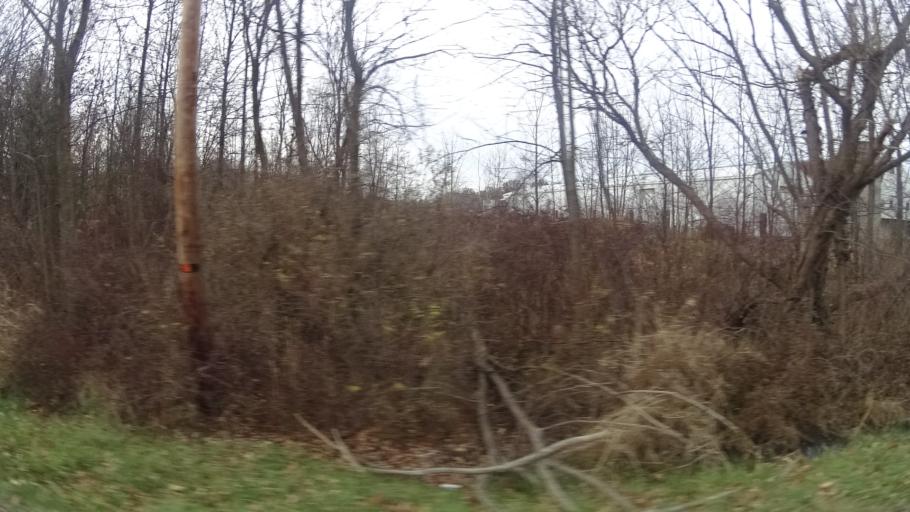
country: US
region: Ohio
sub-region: Lorain County
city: Eaton Estates
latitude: 41.3151
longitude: -81.9461
